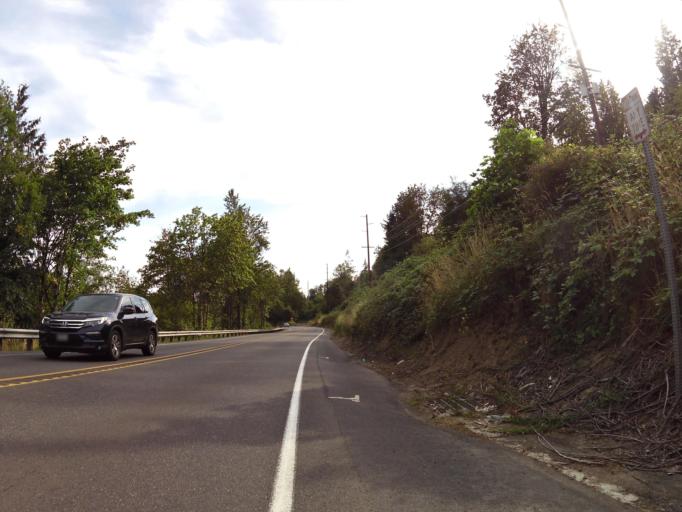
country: US
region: Washington
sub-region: Cowlitz County
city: West Side Highway
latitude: 46.1729
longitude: -122.9148
